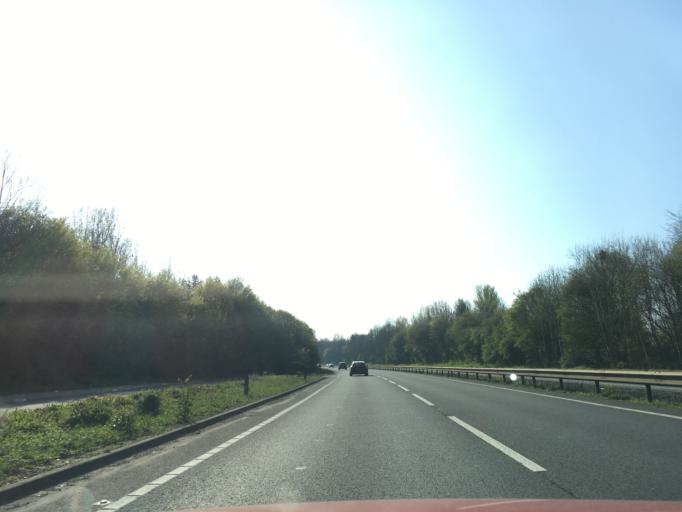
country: GB
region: England
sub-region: Milton Keynes
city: Stony Stratford
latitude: 52.0536
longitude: -0.8342
